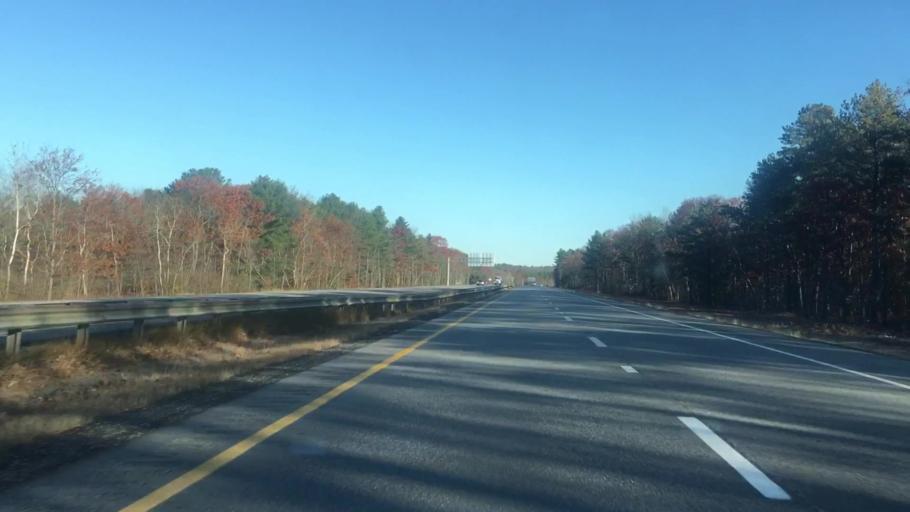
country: US
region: Maine
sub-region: Cumberland County
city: New Gloucester
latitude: 43.9434
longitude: -70.3336
